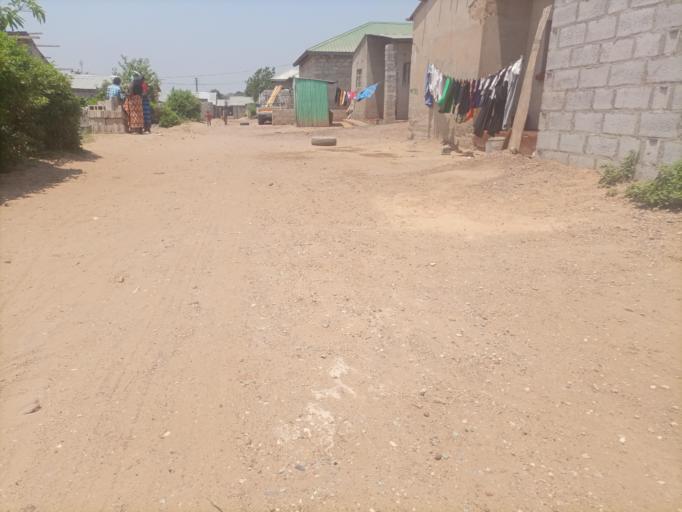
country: ZM
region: Lusaka
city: Lusaka
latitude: -15.4072
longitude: 28.3761
